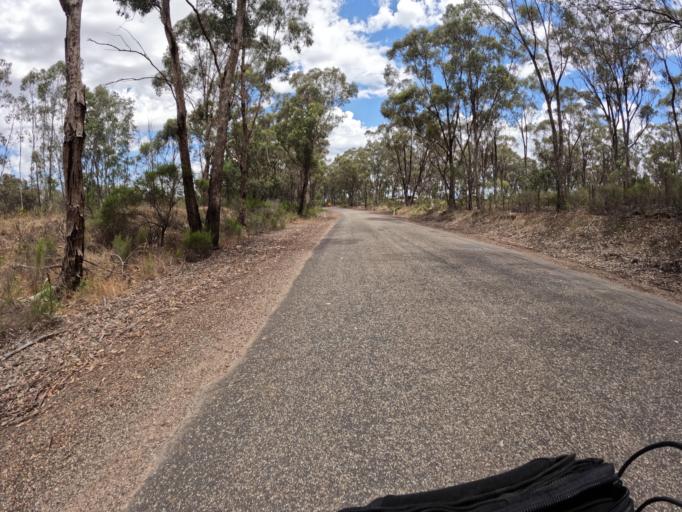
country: AU
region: Victoria
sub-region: Greater Shepparton
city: Shepparton
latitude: -36.6917
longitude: 145.1758
